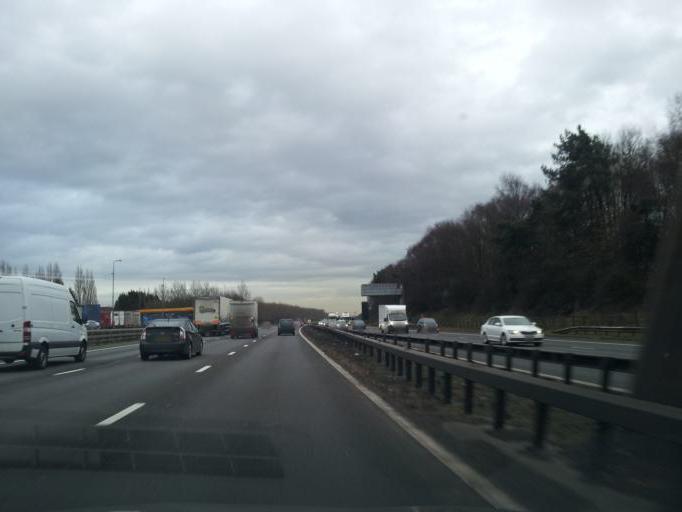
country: GB
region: England
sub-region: Coventry
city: Keresley
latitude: 52.4716
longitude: -1.5464
